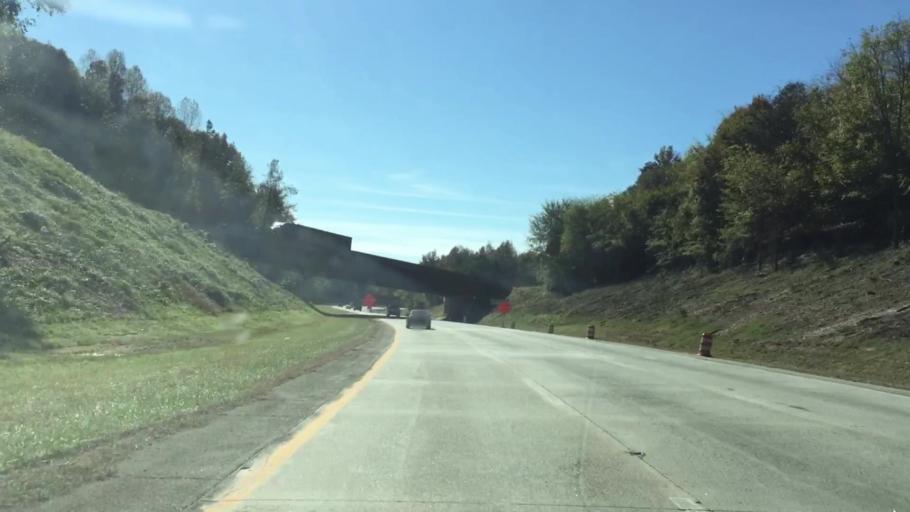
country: US
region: North Carolina
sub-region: Davidson County
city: Thomasville
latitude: 35.8503
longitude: -80.1177
